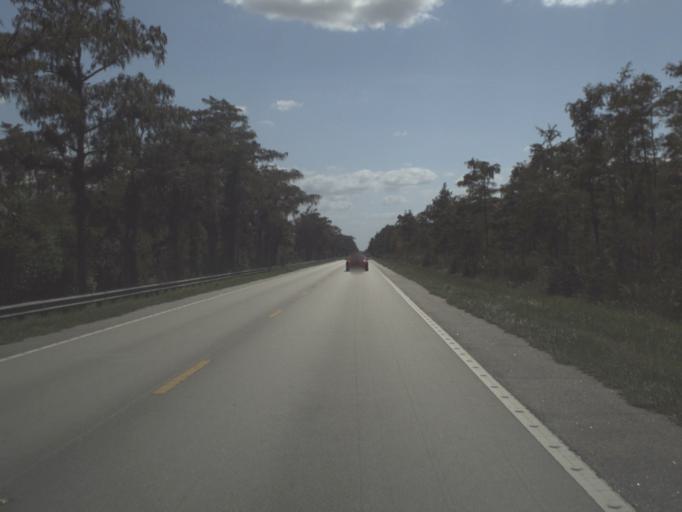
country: US
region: Florida
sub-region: Miami-Dade County
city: Kendall West
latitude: 25.8291
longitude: -80.9007
